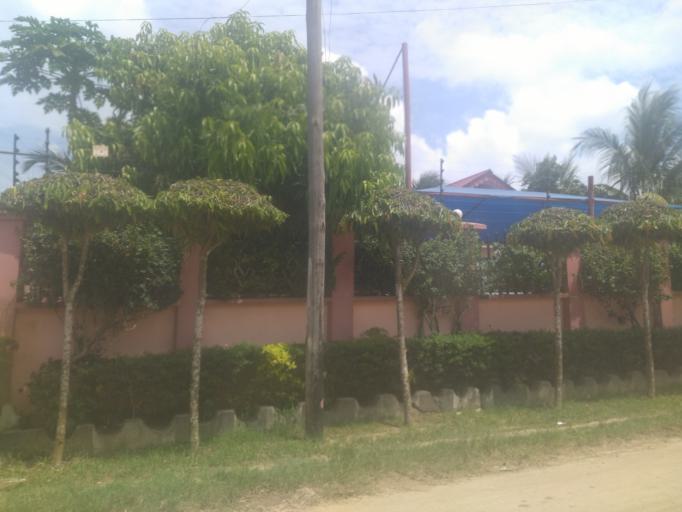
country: TZ
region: Zanzibar Urban/West
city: Zanzibar
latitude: -6.2296
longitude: 39.2181
